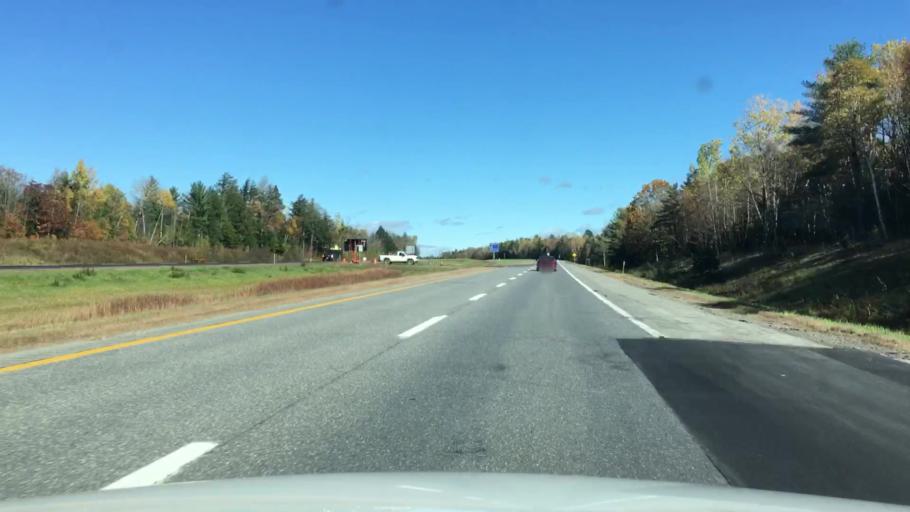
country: US
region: Maine
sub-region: Penobscot County
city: Medway
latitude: 45.6106
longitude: -68.5171
